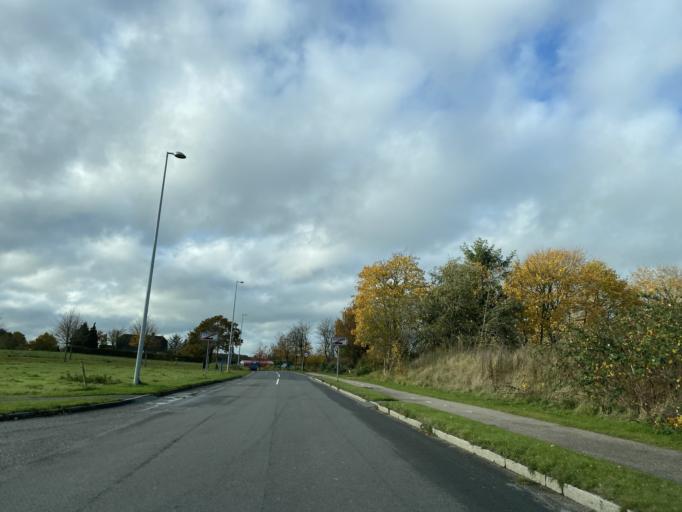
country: DK
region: Central Jutland
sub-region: Favrskov Kommune
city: Hammel
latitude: 56.2554
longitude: 9.8444
